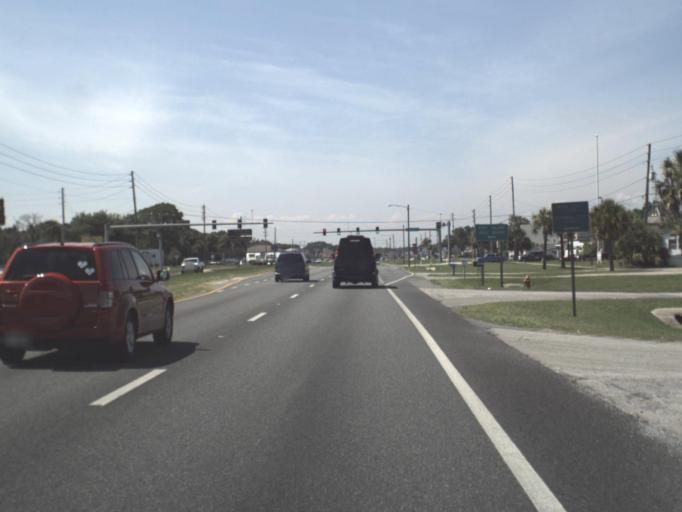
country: US
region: Florida
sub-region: Citrus County
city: Crystal River
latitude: 28.8811
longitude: -82.5819
